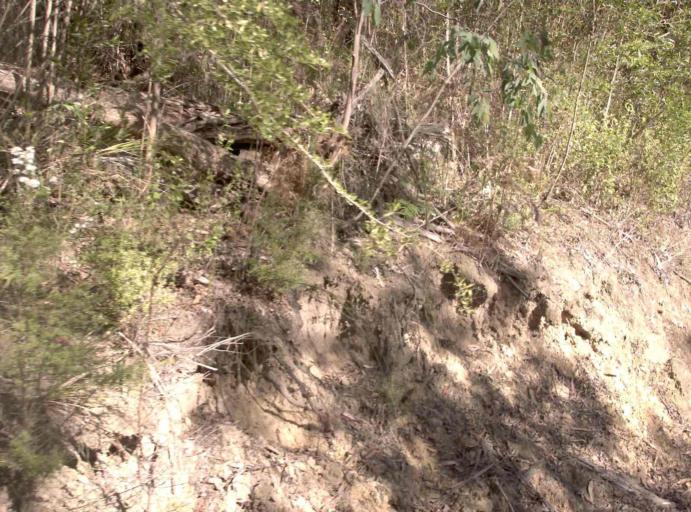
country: AU
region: Victoria
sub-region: East Gippsland
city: Lakes Entrance
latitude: -37.5142
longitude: 148.5484
